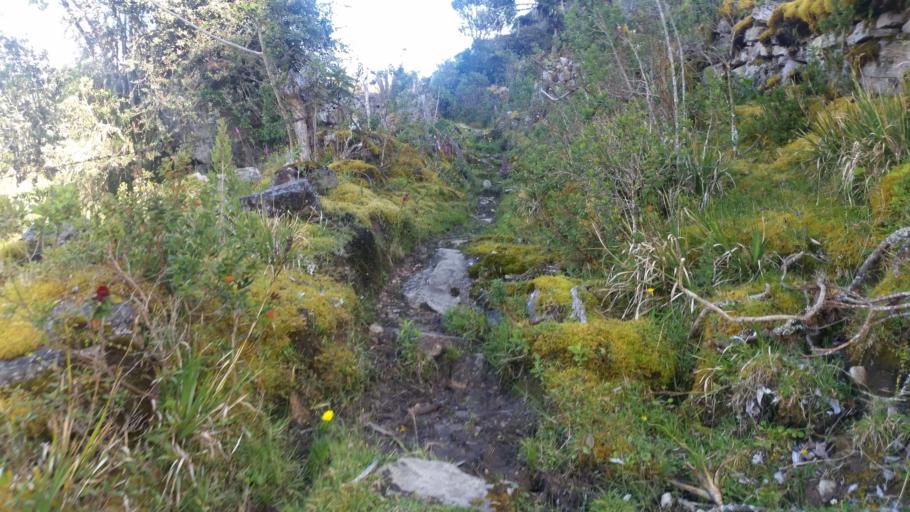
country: CO
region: Cundinamarca
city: Choachi
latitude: 4.5546
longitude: -73.9701
